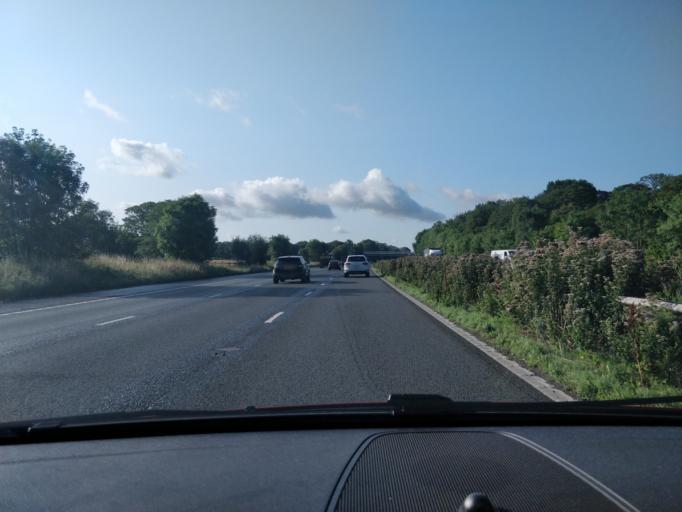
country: GB
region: England
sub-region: Knowsley
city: Knowsley
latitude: 53.4490
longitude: -2.8622
